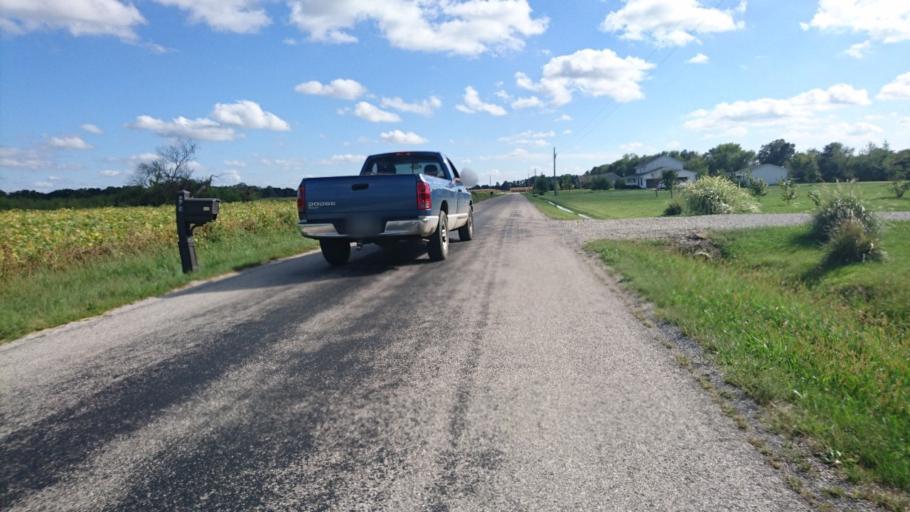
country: US
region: Illinois
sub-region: Macoupin County
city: Staunton
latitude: 39.0054
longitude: -89.7314
